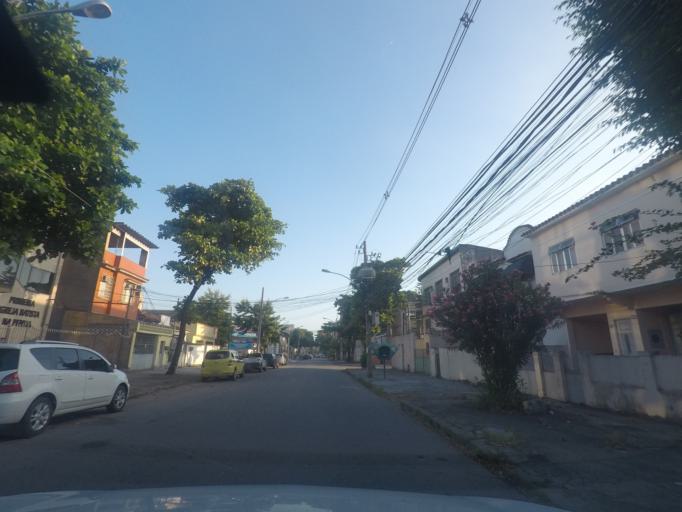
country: BR
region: Rio de Janeiro
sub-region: Duque De Caxias
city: Duque de Caxias
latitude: -22.8353
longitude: -43.2767
